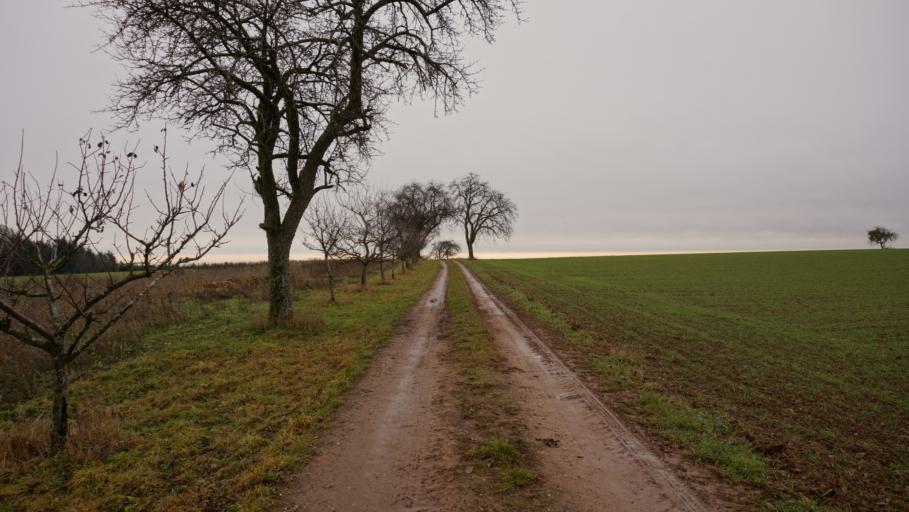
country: DE
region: Baden-Wuerttemberg
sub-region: Karlsruhe Region
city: Fahrenbach
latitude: 49.4465
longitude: 9.1121
